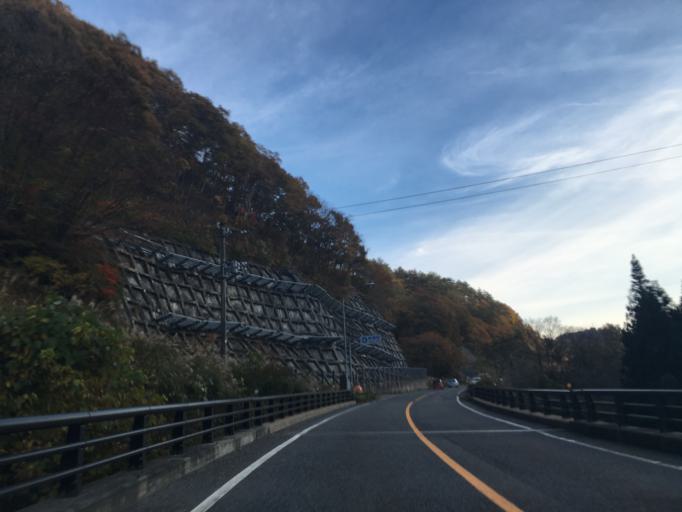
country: JP
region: Fukushima
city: Kitakata
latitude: 37.5738
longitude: 139.7082
